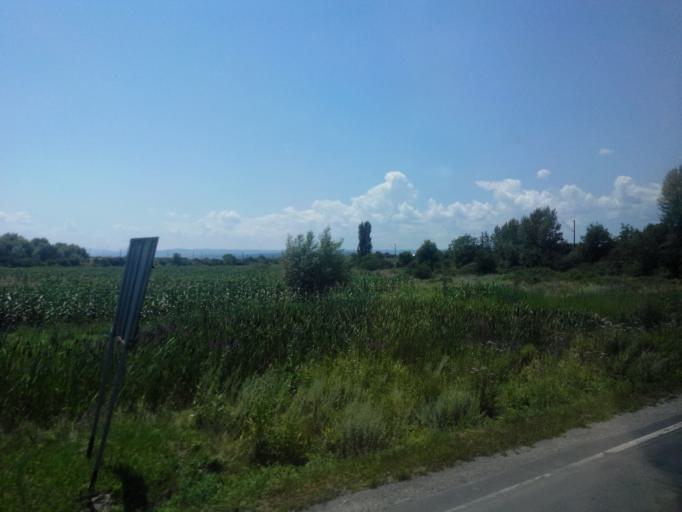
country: RO
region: Hunedoara
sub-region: Oras Simeria
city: Simeria
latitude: 45.8502
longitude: 22.9788
